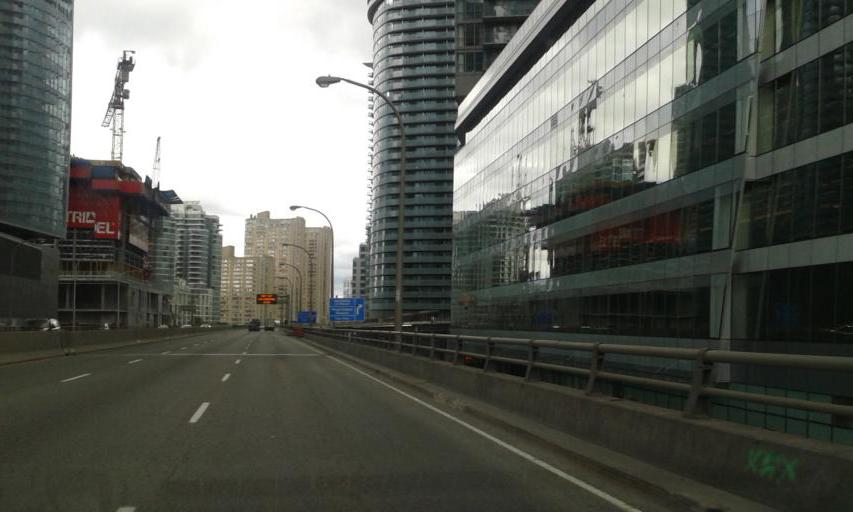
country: CA
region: Ontario
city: Toronto
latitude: 43.6425
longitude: -79.3794
